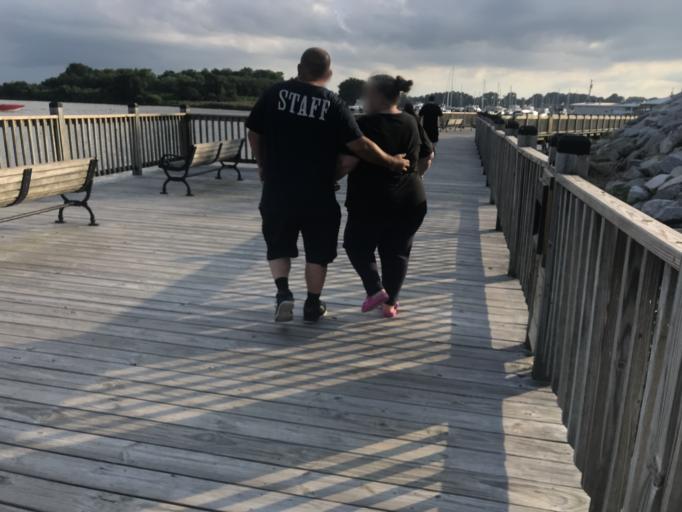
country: US
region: Maryland
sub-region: Harford County
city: Havre de Grace
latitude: 39.5386
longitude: -76.0875
